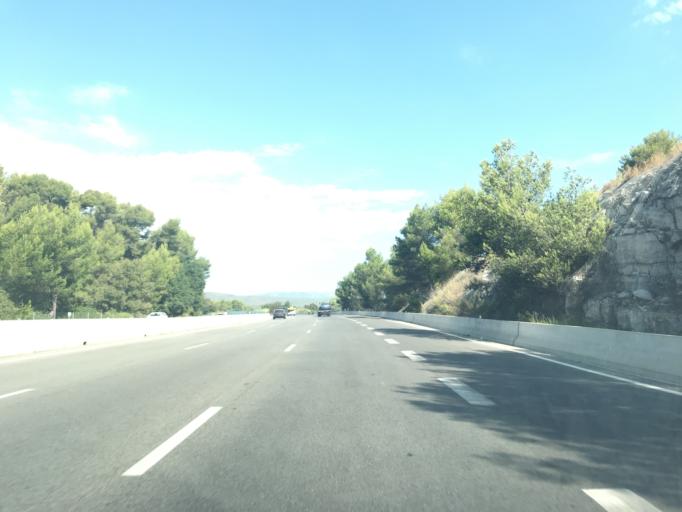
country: FR
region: Provence-Alpes-Cote d'Azur
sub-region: Departement du Var
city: Le Castellet
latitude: 43.1949
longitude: 5.7627
